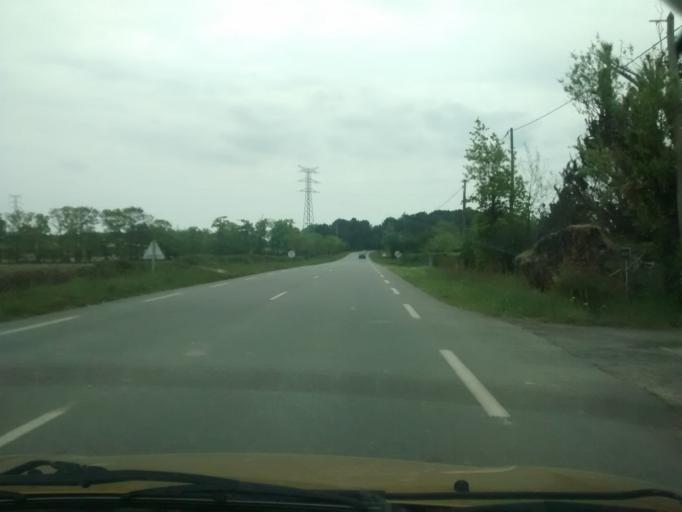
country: FR
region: Brittany
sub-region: Departement du Morbihan
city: Ambon
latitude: 47.5483
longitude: -2.5229
